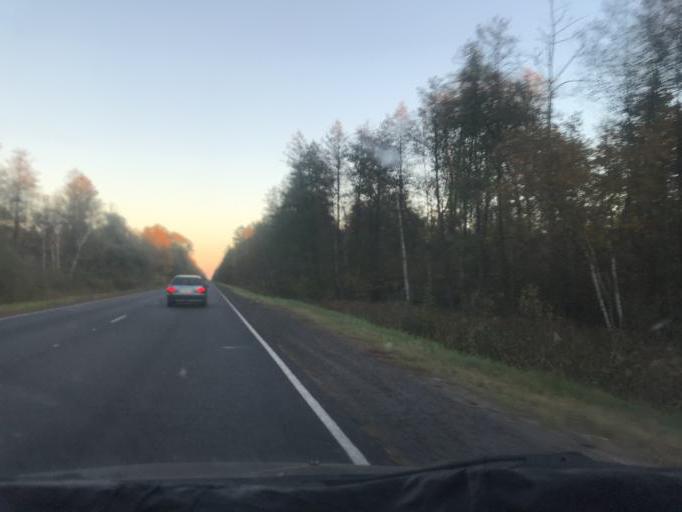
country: BY
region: Gomel
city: Mazyr
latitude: 52.1860
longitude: 29.1437
